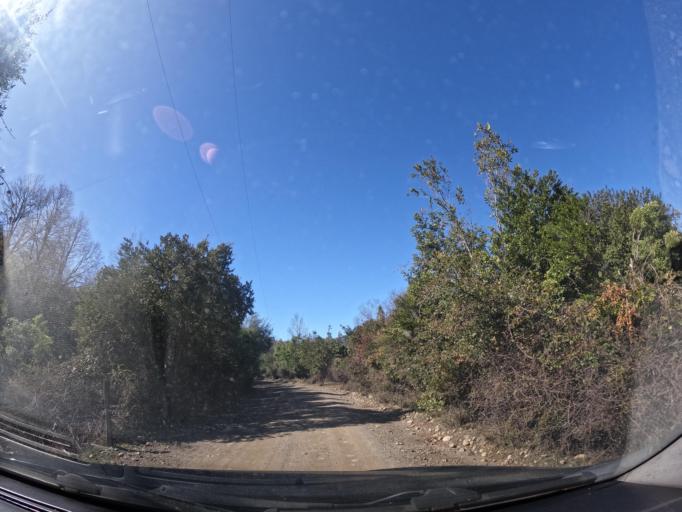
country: CL
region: Maule
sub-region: Provincia de Linares
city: Longavi
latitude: -36.2475
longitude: -71.3333
